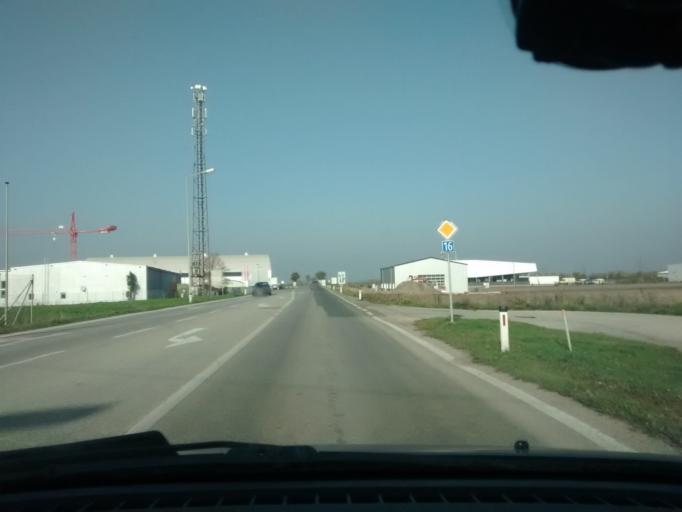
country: AT
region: Lower Austria
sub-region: Politischer Bezirk Modling
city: Munchendorf
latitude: 48.0383
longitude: 16.3800
